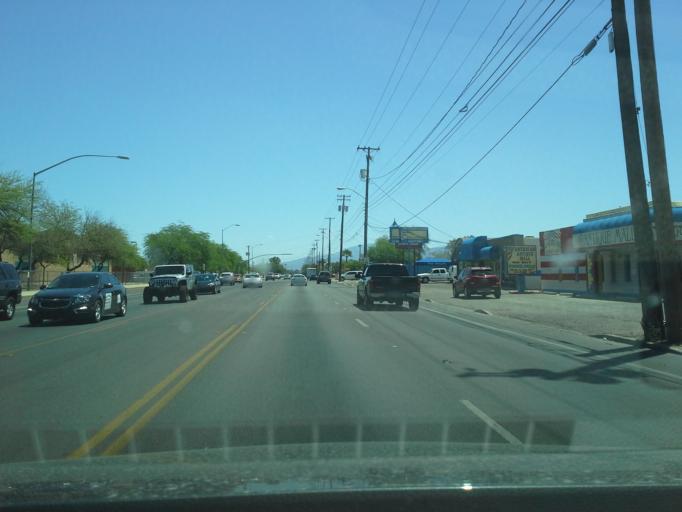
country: US
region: Arizona
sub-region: Pima County
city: Tucson
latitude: 32.2504
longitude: -110.9263
